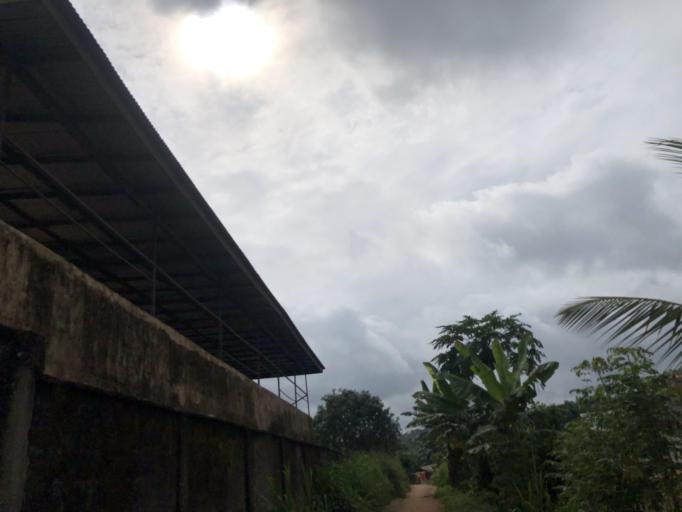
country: SL
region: Eastern Province
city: Kailahun
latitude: 8.2757
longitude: -10.5653
